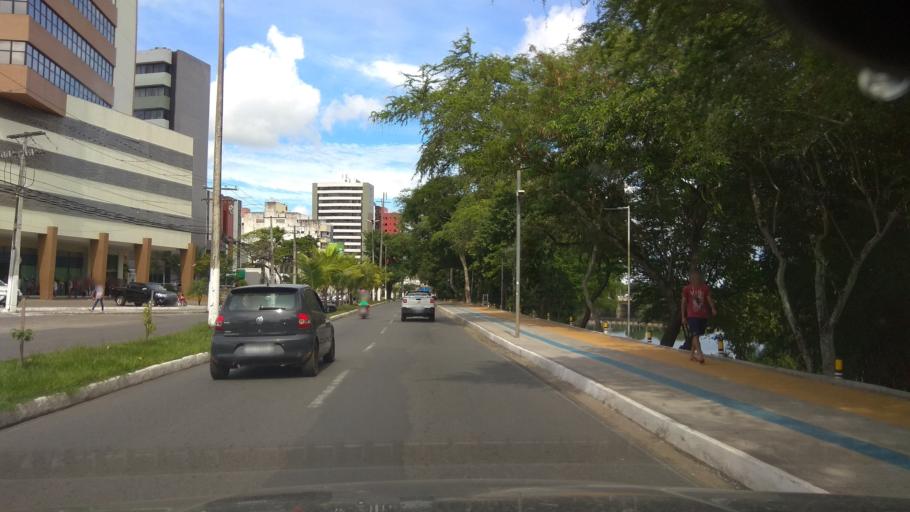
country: BR
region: Bahia
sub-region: Itabuna
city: Itabuna
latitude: -14.7968
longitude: -39.2750
